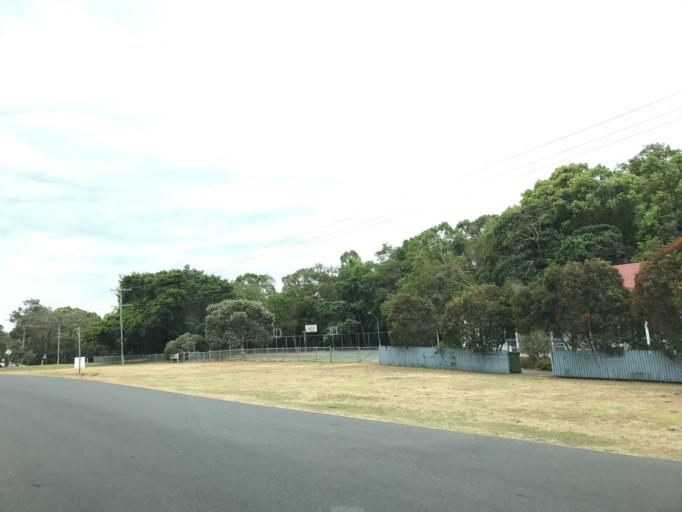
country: AU
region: Queensland
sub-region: Redland
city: Victoria Point
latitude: -27.4958
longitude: 153.4053
